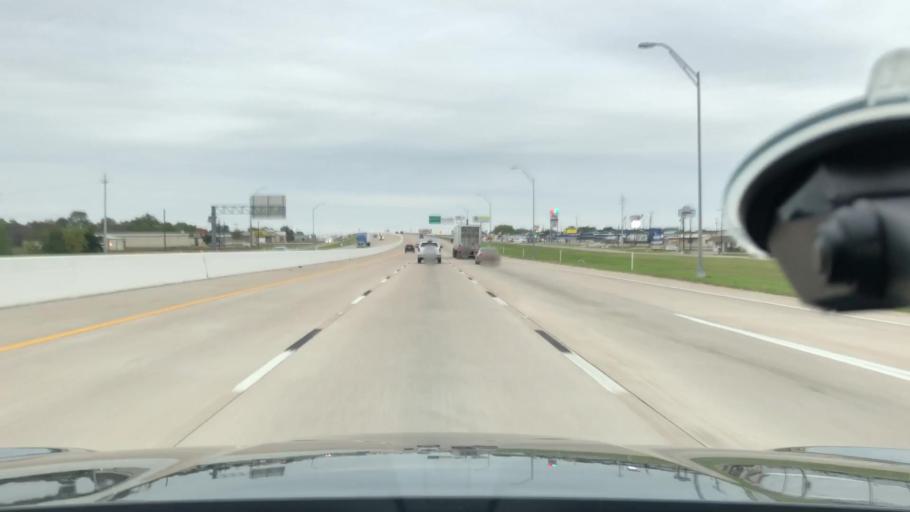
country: US
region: Texas
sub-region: McLennan County
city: Northcrest
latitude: 31.6646
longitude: -97.0999
